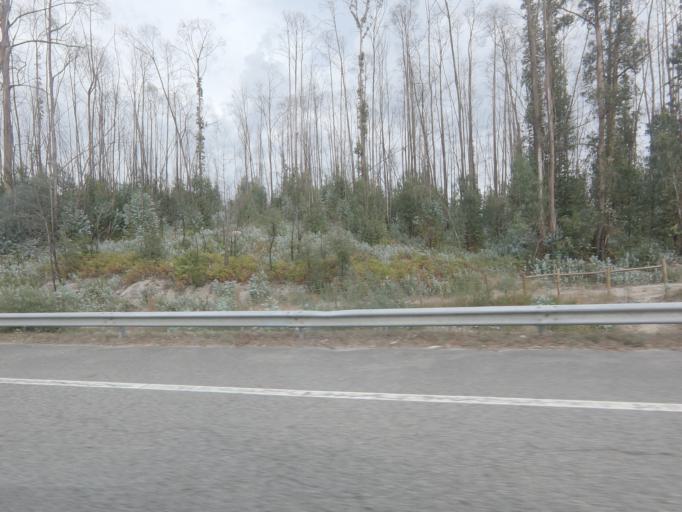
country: PT
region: Viseu
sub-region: Santa Comba Dao
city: Santa Comba Dao
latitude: 40.4428
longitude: -8.1077
